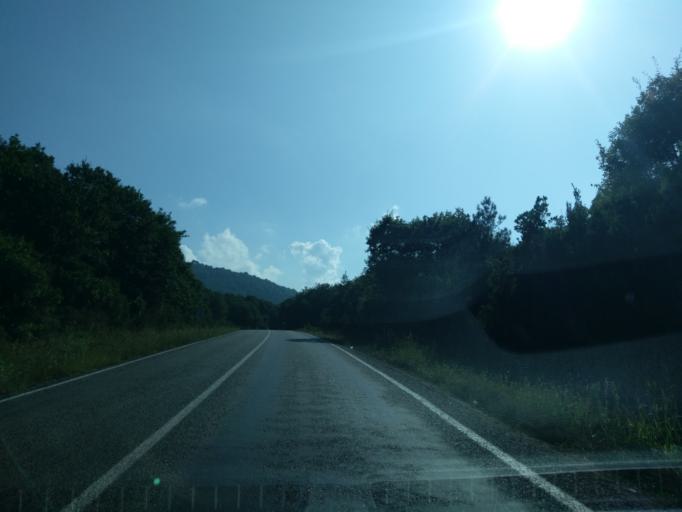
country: TR
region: Sinop
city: Yenikonak
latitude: 41.9462
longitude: 34.7429
